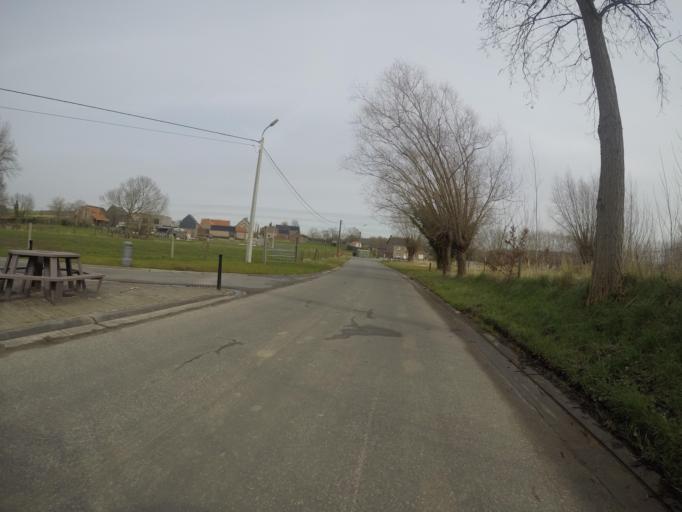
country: BE
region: Flanders
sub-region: Provincie Oost-Vlaanderen
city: Sint-Maria-Lierde
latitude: 50.8240
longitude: 3.8562
